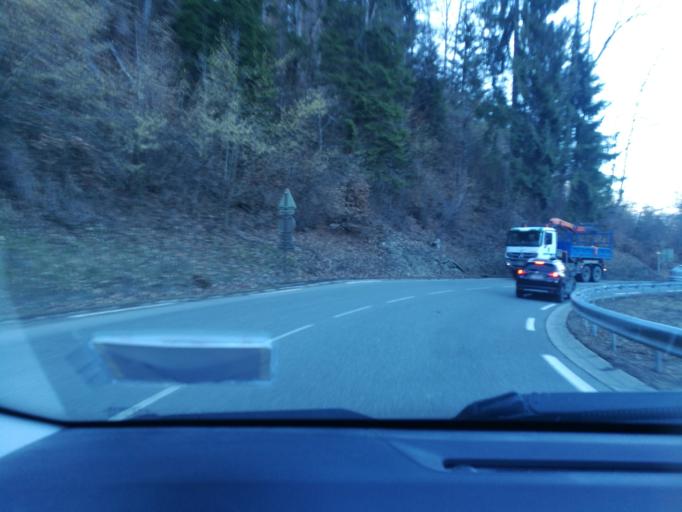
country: FR
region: Rhone-Alpes
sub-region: Departement de la Haute-Savoie
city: Domancy
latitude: 45.9065
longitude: 6.6406
